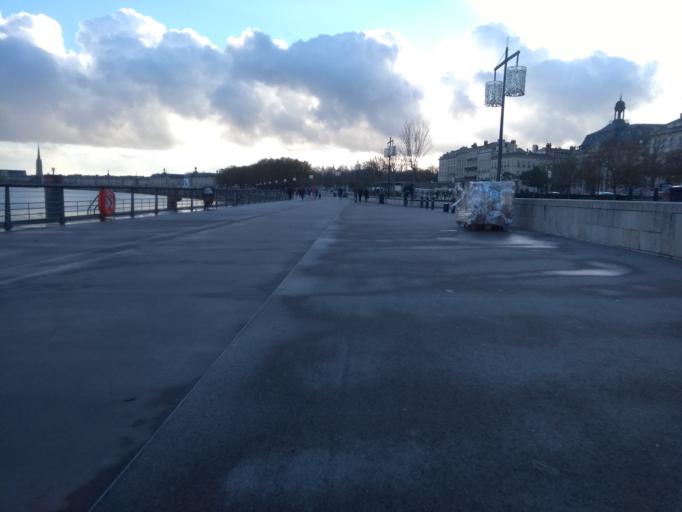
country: FR
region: Aquitaine
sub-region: Departement de la Gironde
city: Bordeaux
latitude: 44.8497
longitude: -0.5694
